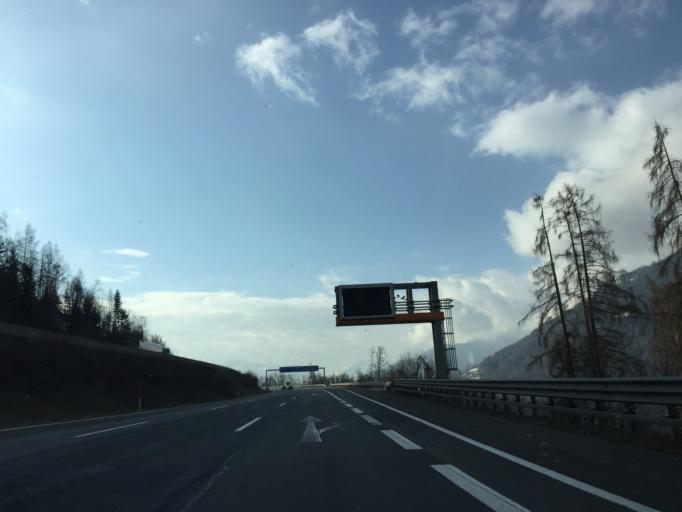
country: AT
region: Salzburg
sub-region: Politischer Bezirk Sankt Johann im Pongau
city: Pfarrwerfen
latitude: 47.4484
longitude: 13.2178
